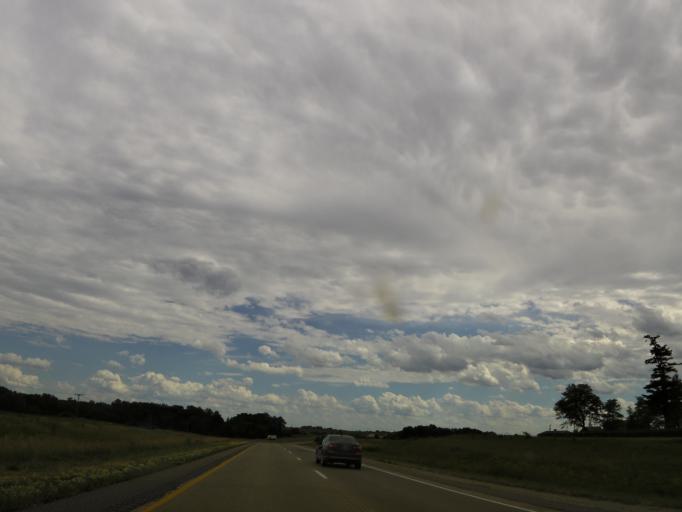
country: US
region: Iowa
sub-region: Henry County
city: Mount Pleasant
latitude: 41.0449
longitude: -91.5450
